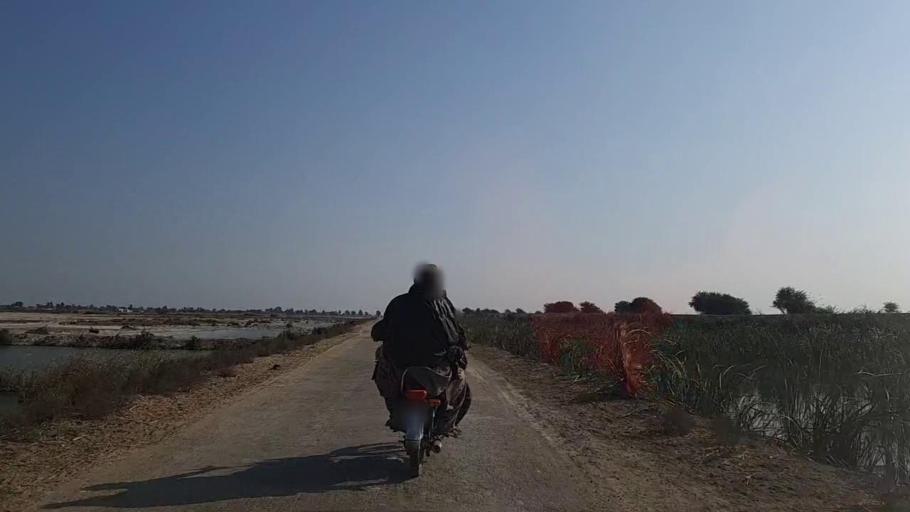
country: PK
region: Sindh
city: Sanghar
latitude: 25.9795
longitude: 69.0246
